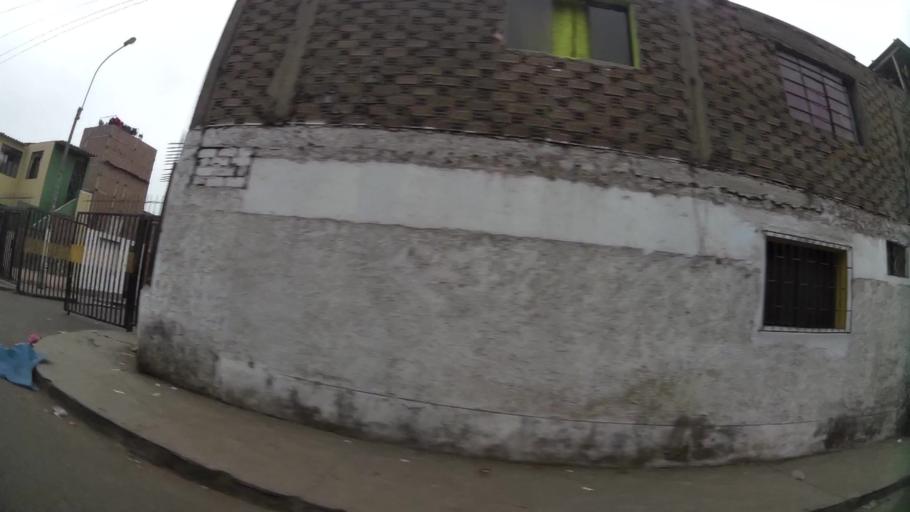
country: PE
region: Lima
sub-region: Lima
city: Surco
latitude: -12.1500
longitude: -76.9769
